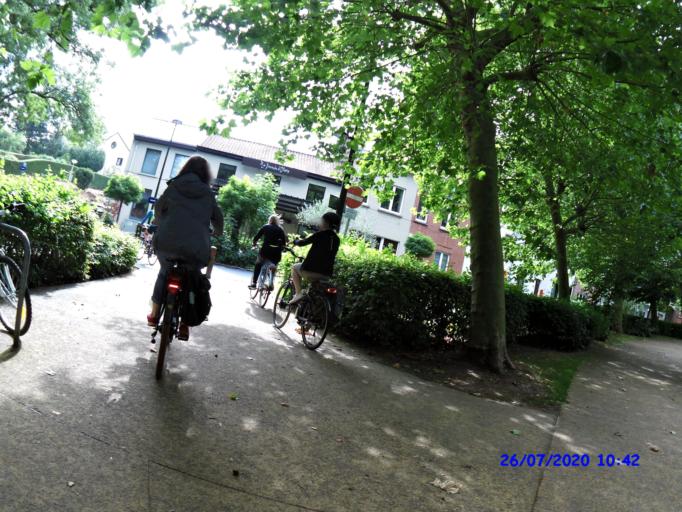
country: BE
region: Flanders
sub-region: Provincie Vlaams-Brabant
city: Linkebeek
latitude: 50.7879
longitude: 4.3393
